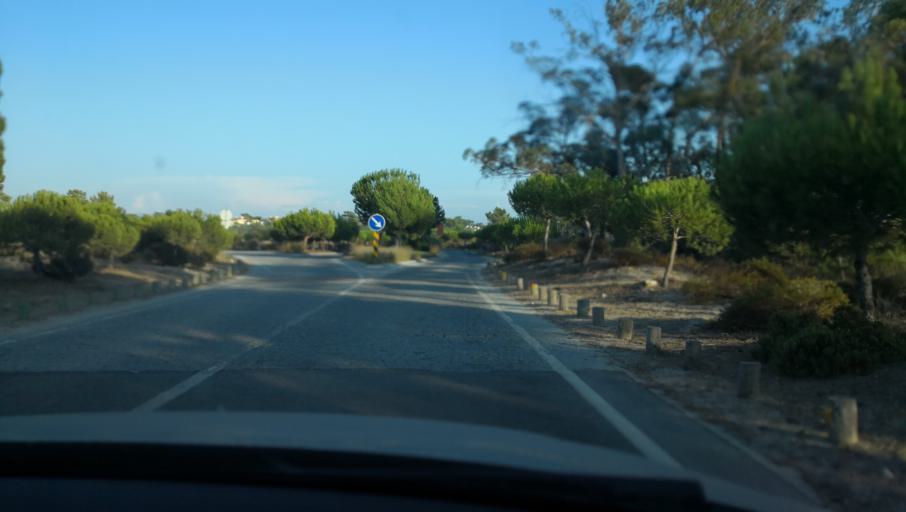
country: PT
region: Setubal
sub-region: Setubal
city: Setubal
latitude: 38.4652
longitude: -8.8714
